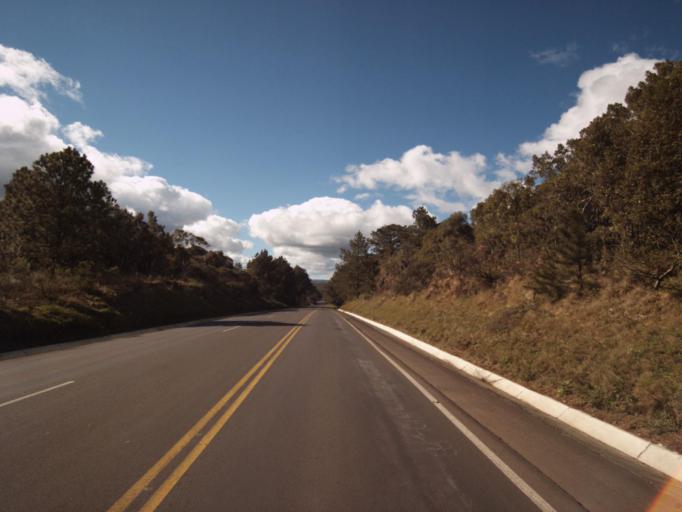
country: BR
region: Santa Catarina
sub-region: Joacaba
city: Joacaba
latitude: -26.9812
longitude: -51.7861
